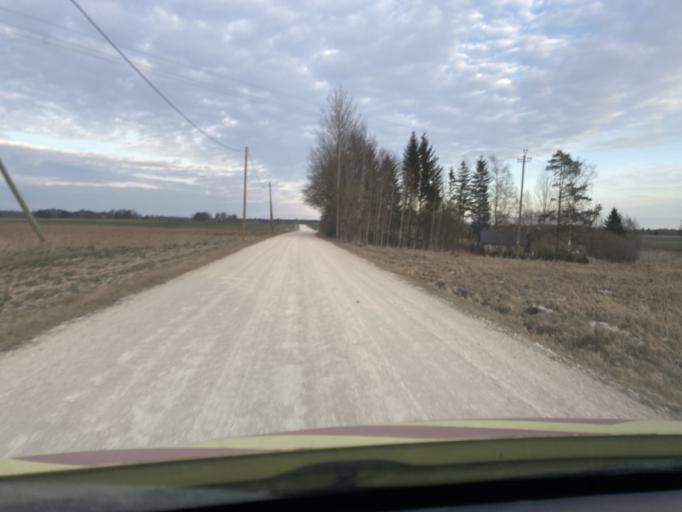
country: EE
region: Jogevamaa
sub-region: Poltsamaa linn
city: Poltsamaa
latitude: 58.5922
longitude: 26.1945
